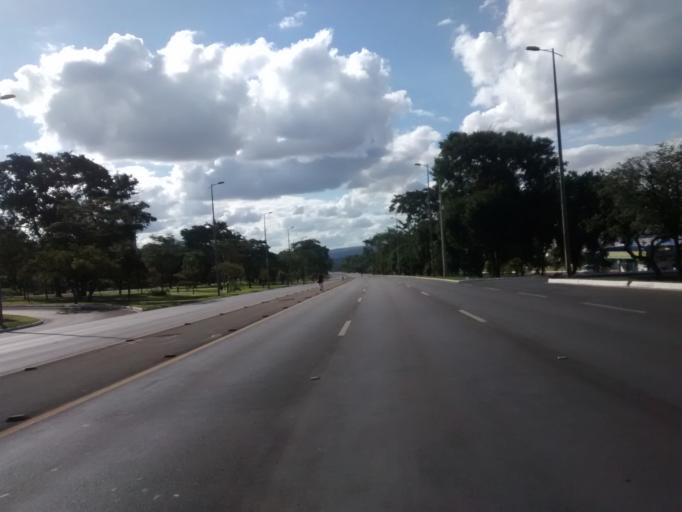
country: BR
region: Federal District
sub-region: Brasilia
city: Brasilia
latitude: -15.7696
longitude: -47.8820
